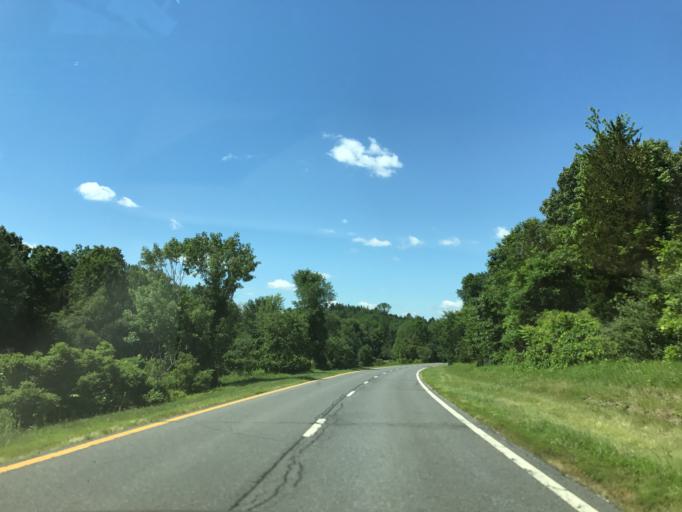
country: US
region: New York
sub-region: Dutchess County
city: Pine Plains
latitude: 41.9320
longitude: -73.7569
